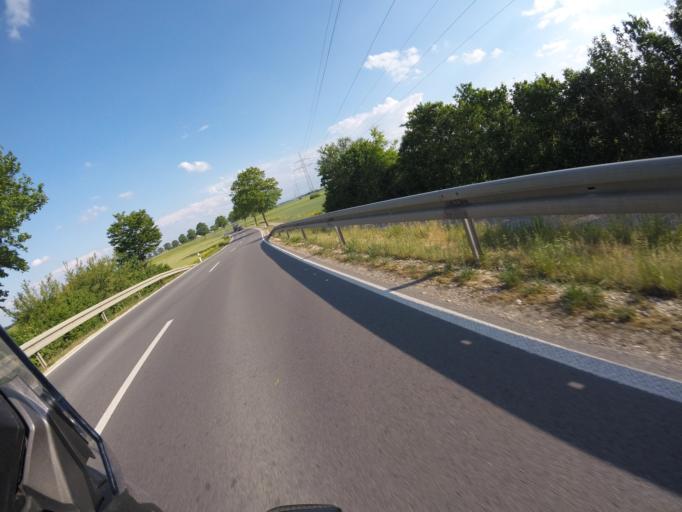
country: DE
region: Bavaria
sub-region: Upper Bavaria
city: Eching
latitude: 48.2942
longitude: 11.6358
